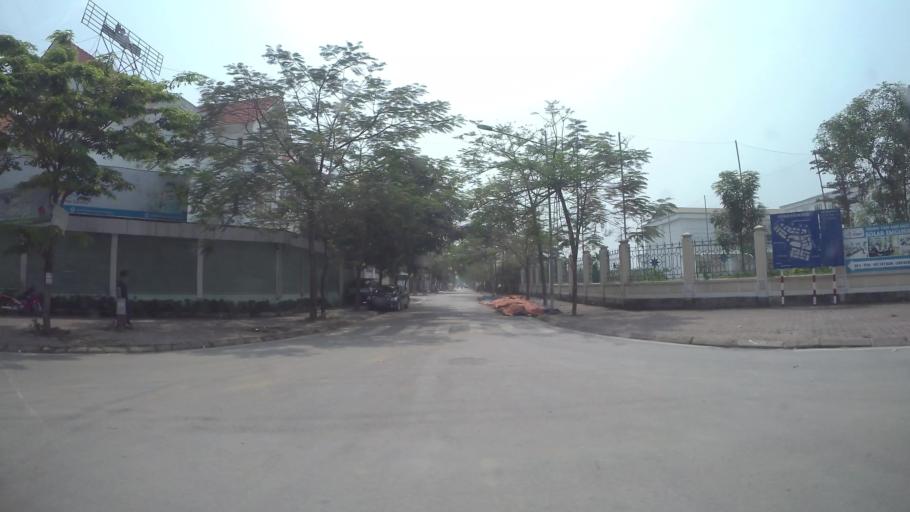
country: VN
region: Ha Noi
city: Van Dien
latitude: 20.9601
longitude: 105.8225
